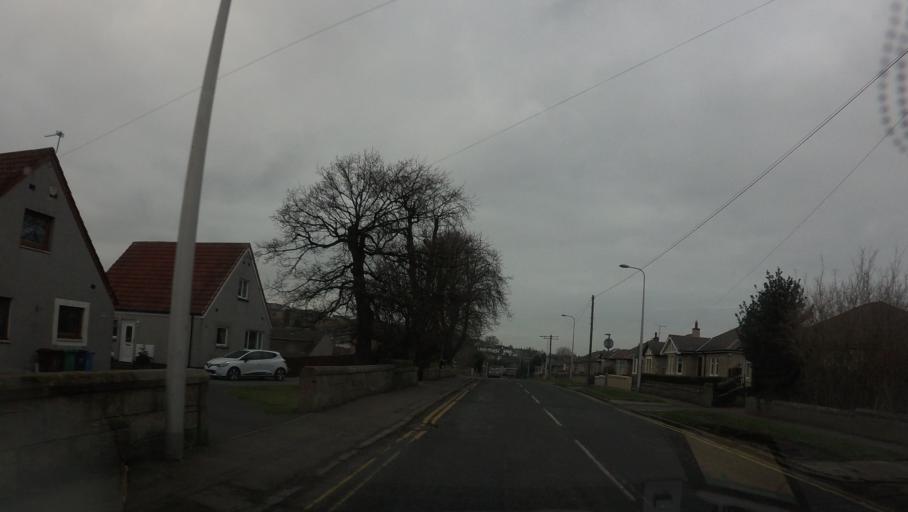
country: GB
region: Scotland
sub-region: Fife
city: Inverkeithing
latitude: 56.0327
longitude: -3.3913
